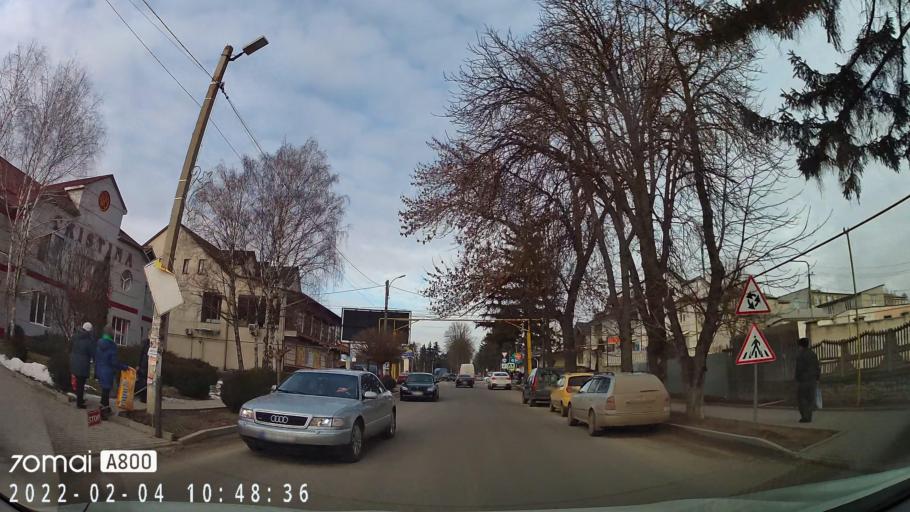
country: MD
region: Briceni
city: Briceni
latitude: 48.3587
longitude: 27.0904
